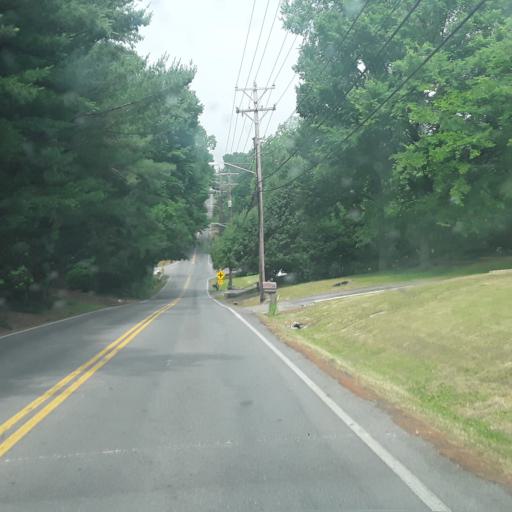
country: US
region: Tennessee
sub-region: Davidson County
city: Oak Hill
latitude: 36.0746
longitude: -86.7489
